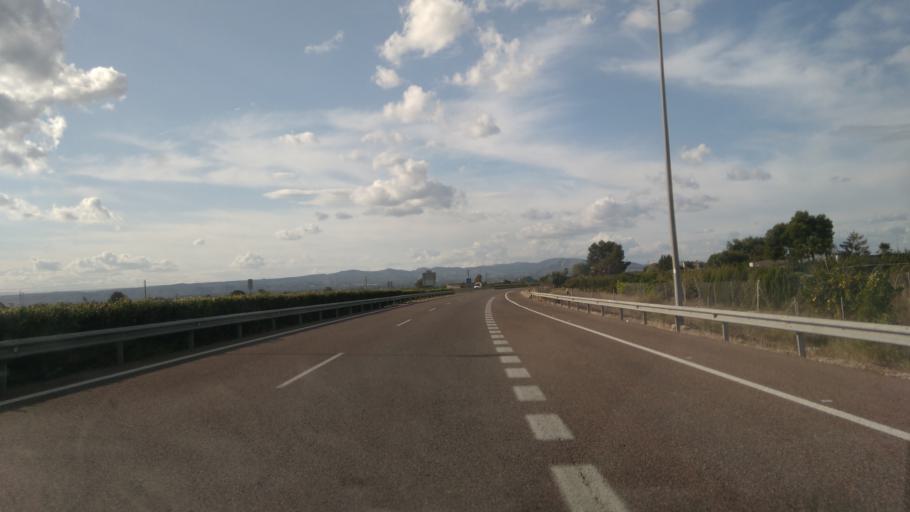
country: ES
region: Valencia
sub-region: Provincia de Valencia
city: Guadassuar
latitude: 39.1781
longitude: -0.4806
